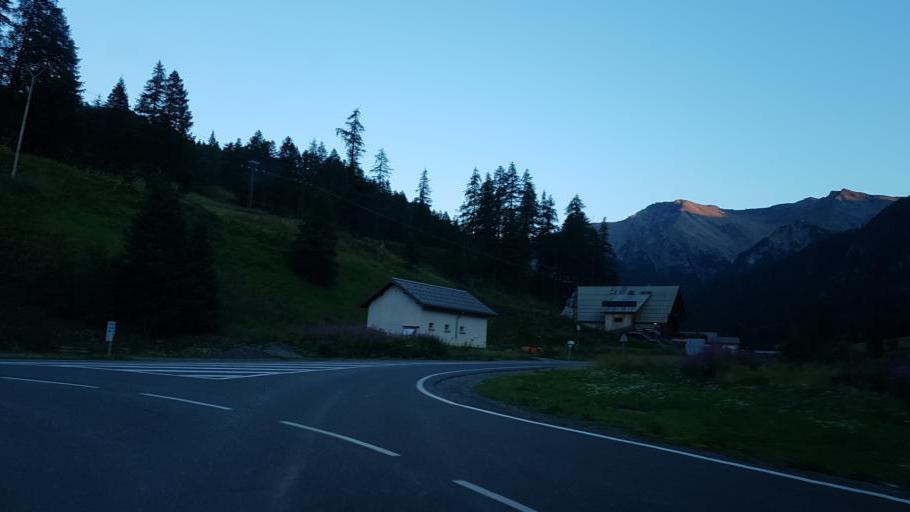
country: IT
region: Piedmont
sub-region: Provincia di Cuneo
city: Pontechianale
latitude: 44.7182
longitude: 6.8476
